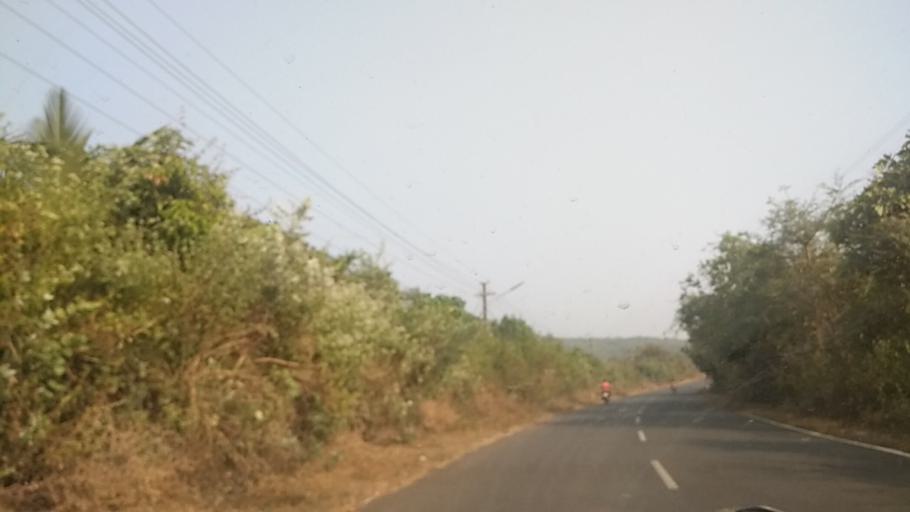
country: IN
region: Goa
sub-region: North Goa
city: Morjim
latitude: 15.6566
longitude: 73.7488
